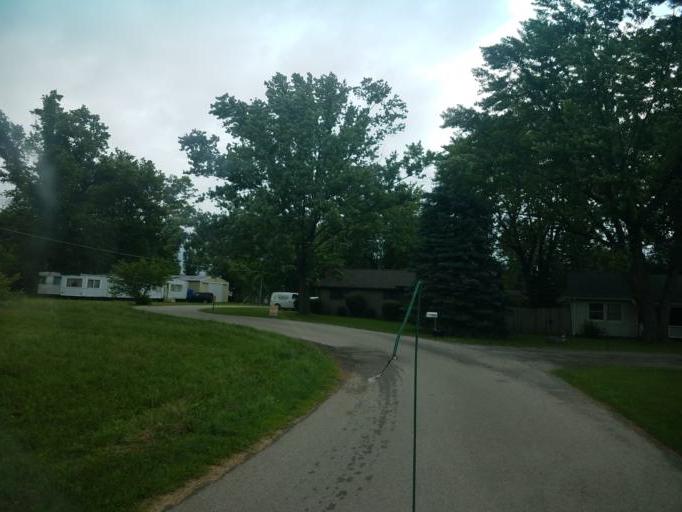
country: US
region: Ohio
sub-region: Logan County
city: Russells Point
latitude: 40.4662
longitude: -83.8728
